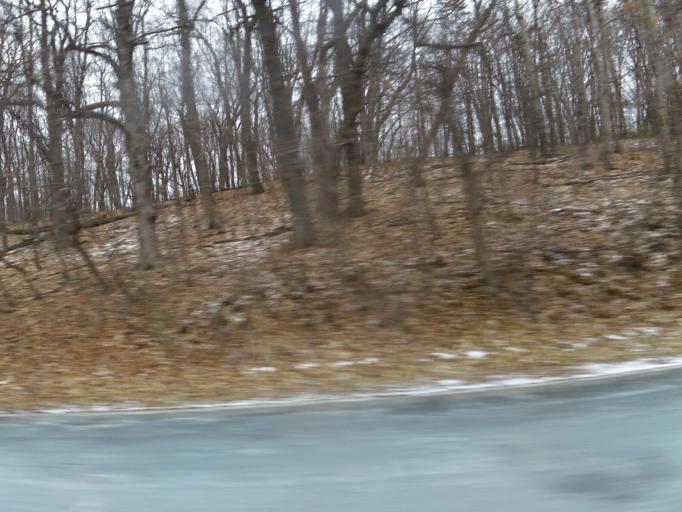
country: US
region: Minnesota
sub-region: Hennepin County
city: Medina
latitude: 45.0236
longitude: -93.5878
